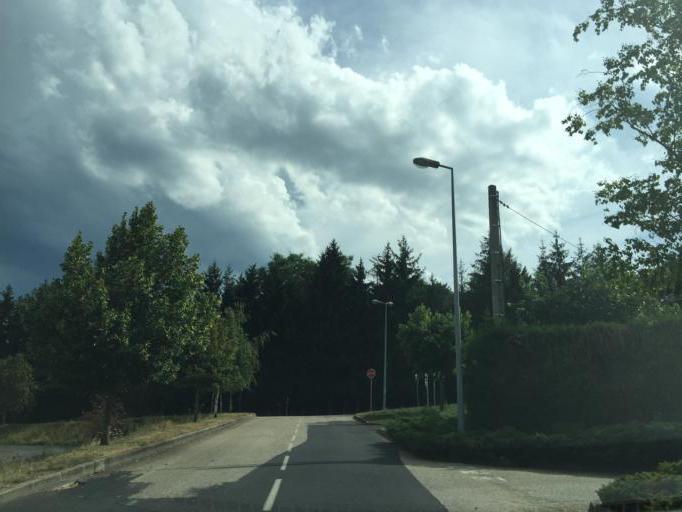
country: FR
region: Rhone-Alpes
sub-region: Departement de la Loire
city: Saint-Jean-Bonnefonds
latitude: 45.4447
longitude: 4.4460
